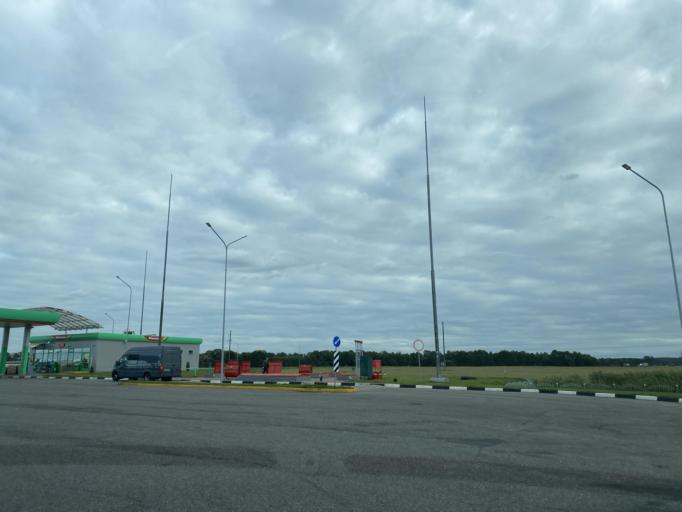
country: BY
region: Grodnenskaya
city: Smarhon'
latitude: 54.4569
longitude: 26.3862
